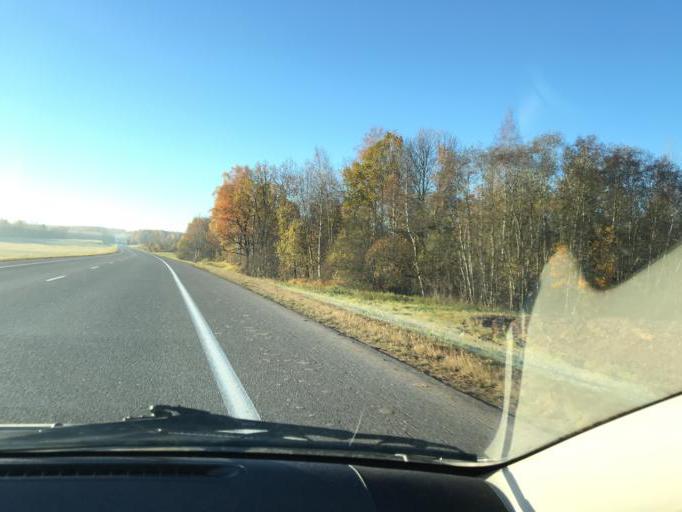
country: BY
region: Vitebsk
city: Vitebsk
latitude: 55.0751
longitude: 30.3079
